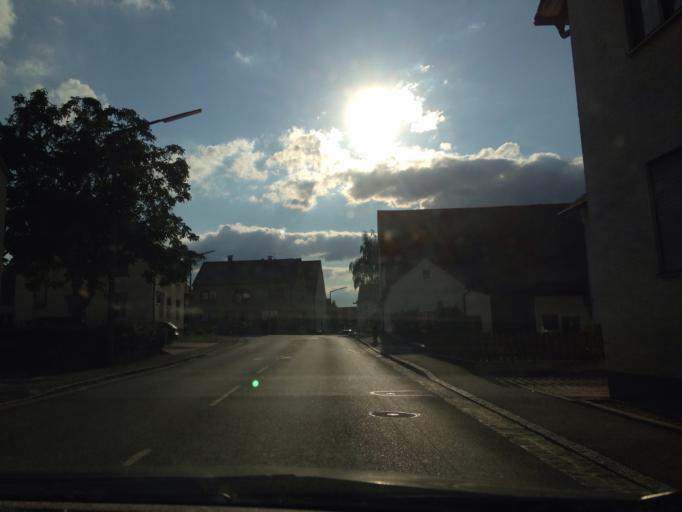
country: DE
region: Bavaria
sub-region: Upper Palatinate
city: Freystadt
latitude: 49.1714
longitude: 11.2873
